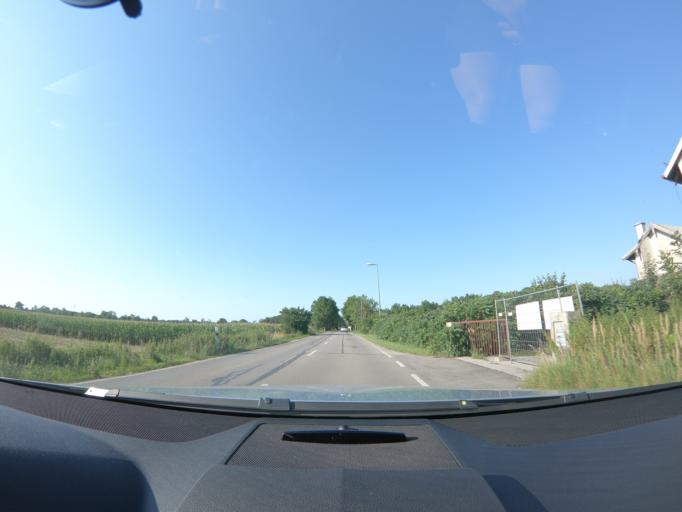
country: DE
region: Bavaria
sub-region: Upper Bavaria
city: Unterhaching
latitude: 48.0890
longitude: 11.6240
